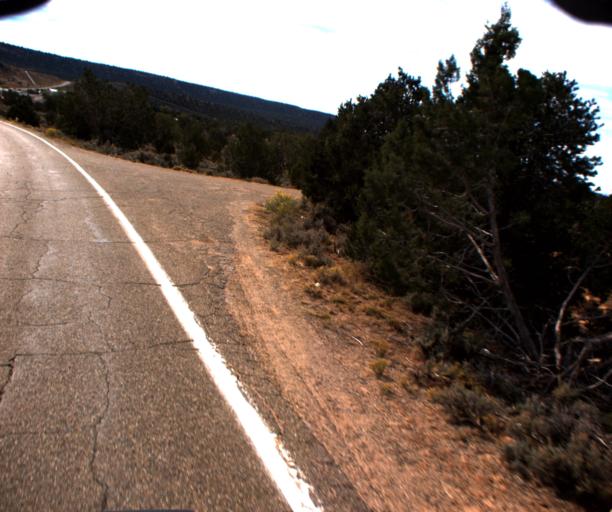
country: US
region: Arizona
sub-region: Navajo County
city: Kayenta
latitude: 36.5636
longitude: -110.5030
